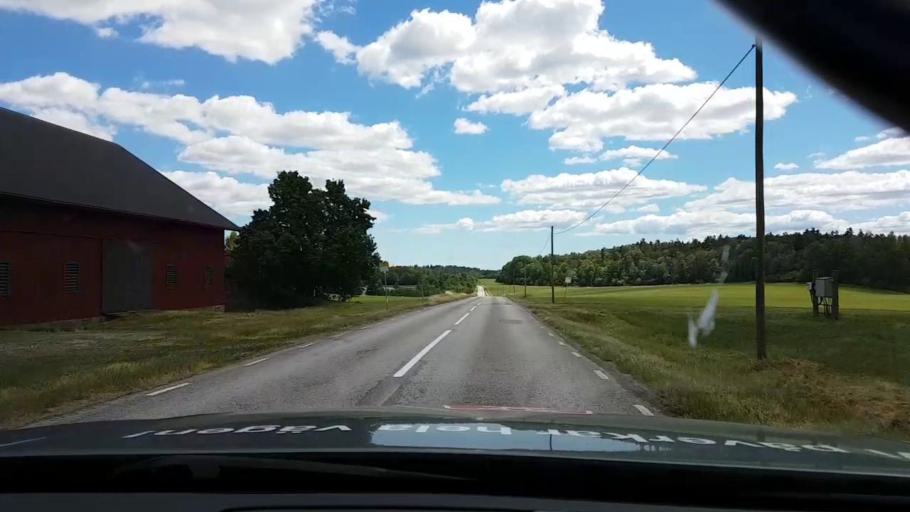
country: SE
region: Kalmar
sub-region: Vasterviks Kommun
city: Forserum
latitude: 58.0469
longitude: 16.4130
